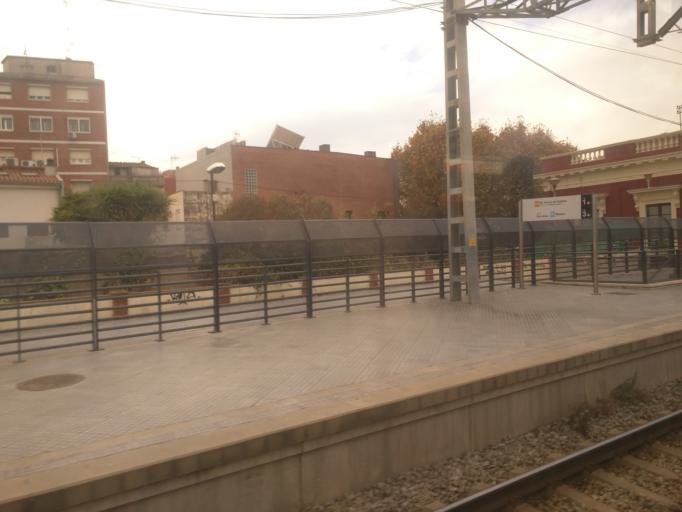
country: ES
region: Catalonia
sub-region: Provincia de Barcelona
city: Molins de Rei
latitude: 41.4095
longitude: 2.0213
